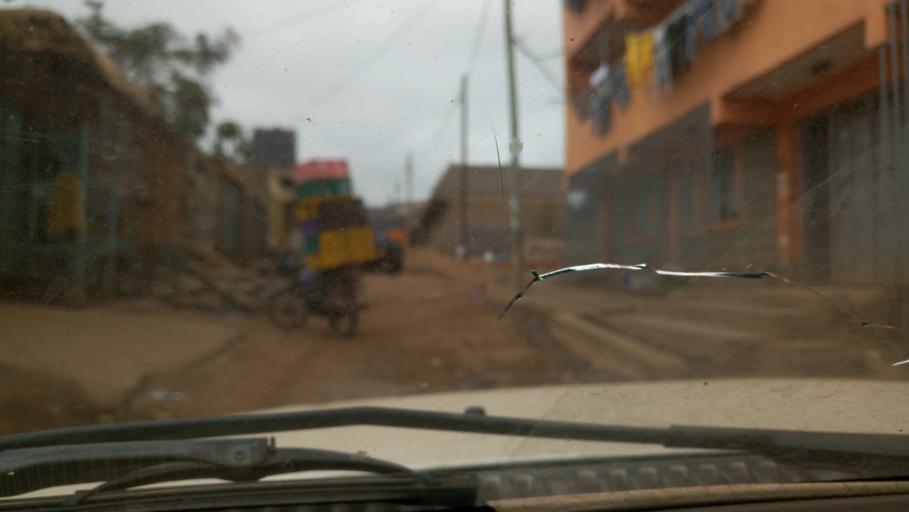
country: KE
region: Nairobi Area
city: Pumwani
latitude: -1.2516
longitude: 36.9192
